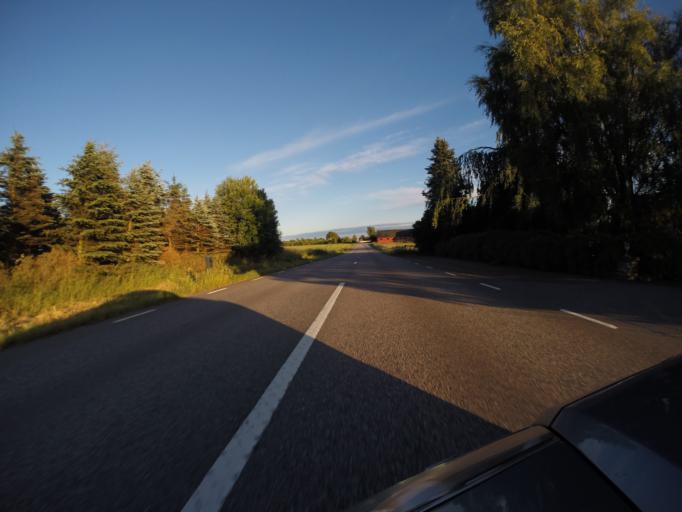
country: SE
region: Skane
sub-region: Angelholms Kommun
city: Strovelstorp
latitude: 56.1557
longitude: 12.8641
